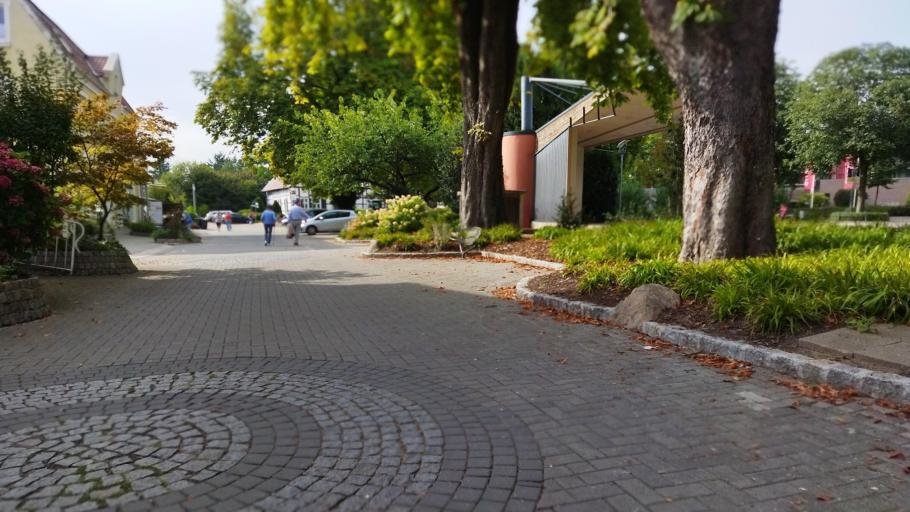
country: DE
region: Lower Saxony
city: Bad Laer
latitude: 52.1010
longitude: 8.0889
